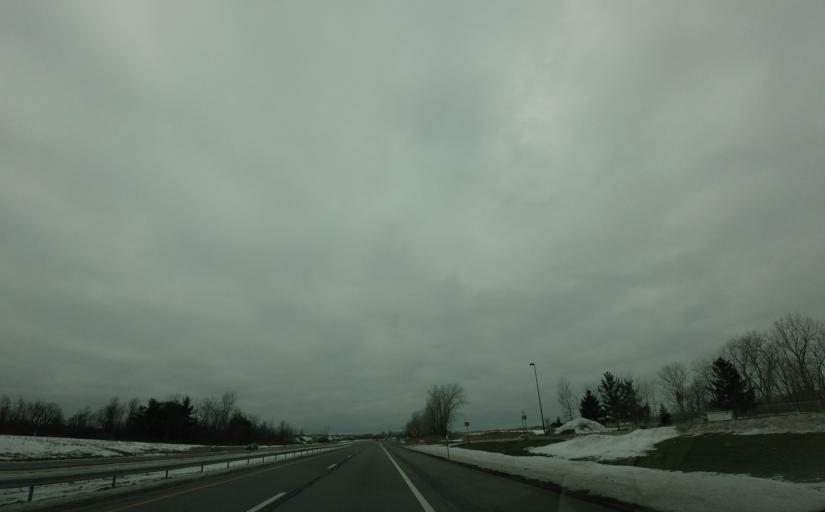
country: US
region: New York
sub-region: Erie County
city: Clarence
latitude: 42.9519
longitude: -78.6037
